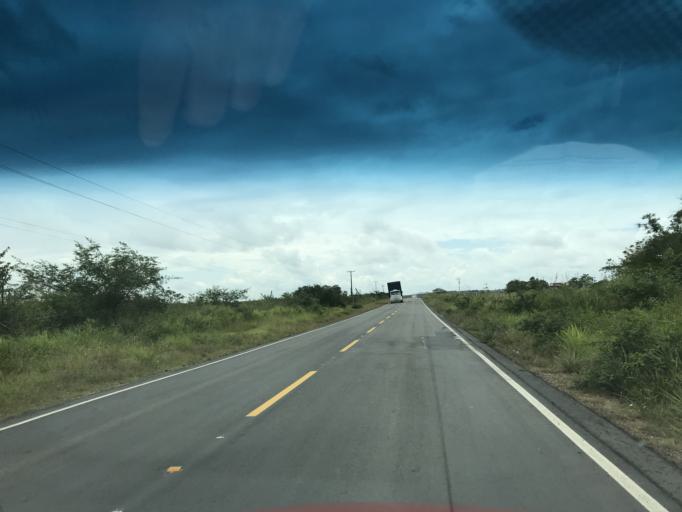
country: BR
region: Bahia
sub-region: Castro Alves
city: Castro Alves
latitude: -12.6828
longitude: -39.3062
